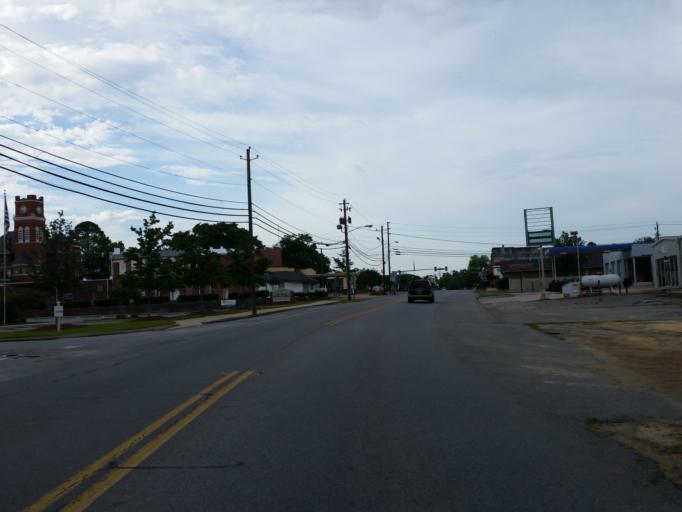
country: US
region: Georgia
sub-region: Dooly County
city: Vienna
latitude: 32.0894
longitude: -83.7966
